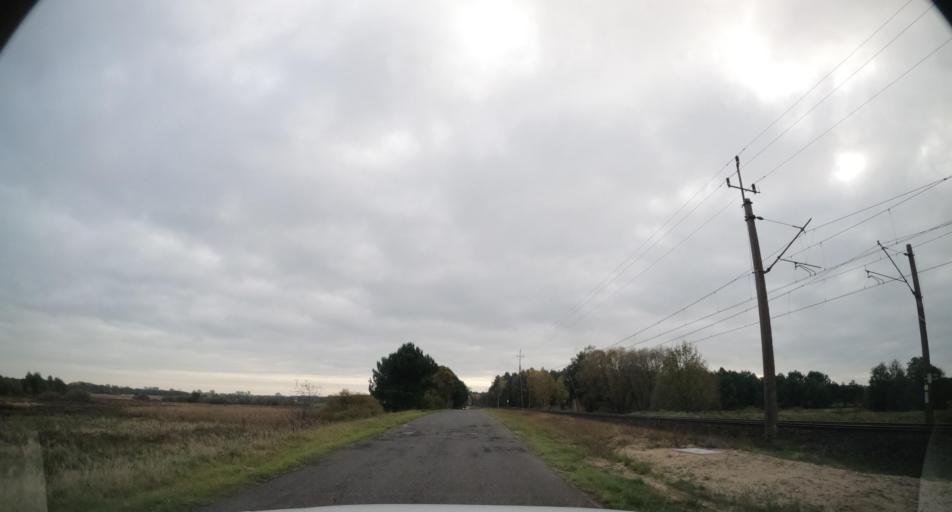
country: PL
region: West Pomeranian Voivodeship
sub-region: Powiat kamienski
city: Miedzyzdroje
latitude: 53.9240
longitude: 14.5520
